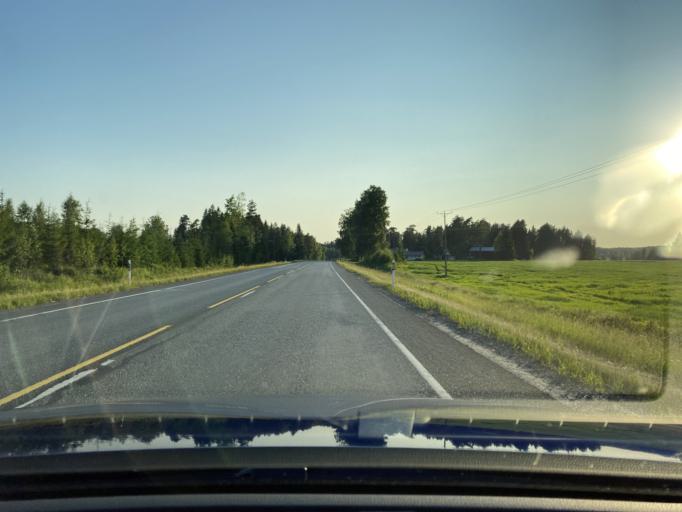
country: FI
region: Haeme
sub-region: Forssa
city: Tammela
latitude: 60.8256
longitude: 23.9815
